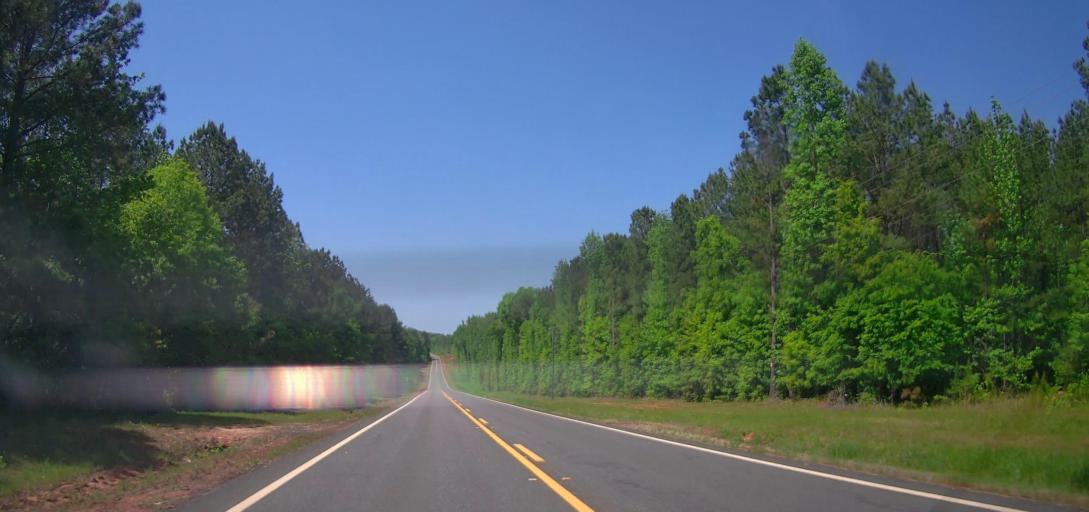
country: US
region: Georgia
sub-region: Jasper County
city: Monticello
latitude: 33.2443
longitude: -83.5562
